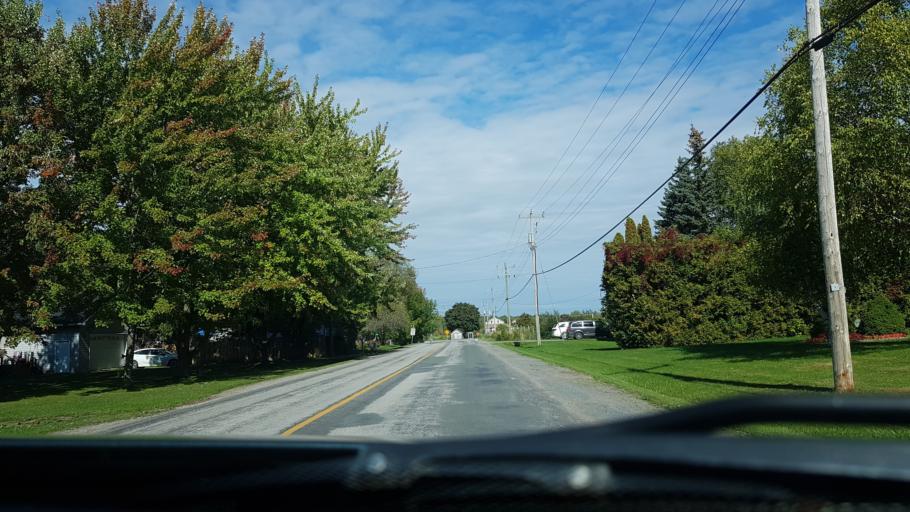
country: CA
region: Ontario
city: Orillia
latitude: 44.5979
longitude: -79.3198
